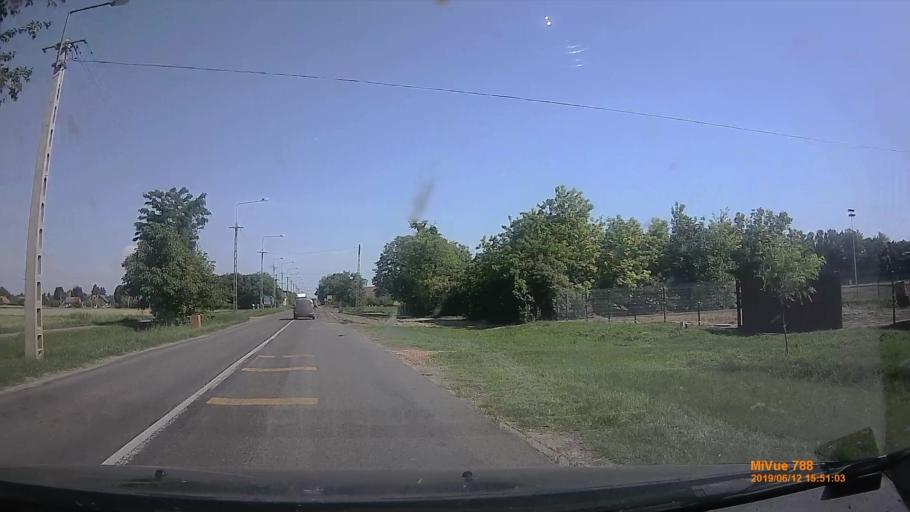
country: HU
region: Csongrad
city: Apatfalva
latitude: 46.1830
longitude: 20.5694
